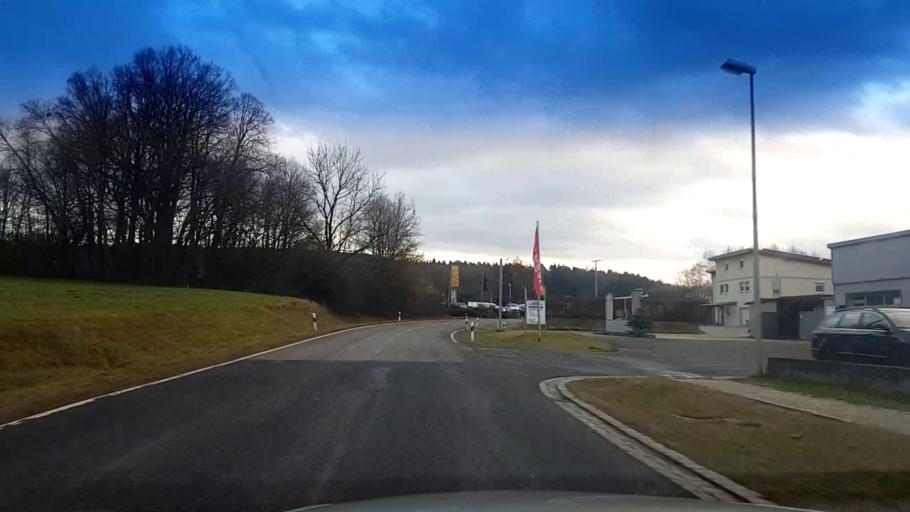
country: DE
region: Bavaria
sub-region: Upper Franconia
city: Litzendorf
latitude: 49.8679
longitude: 11.0252
